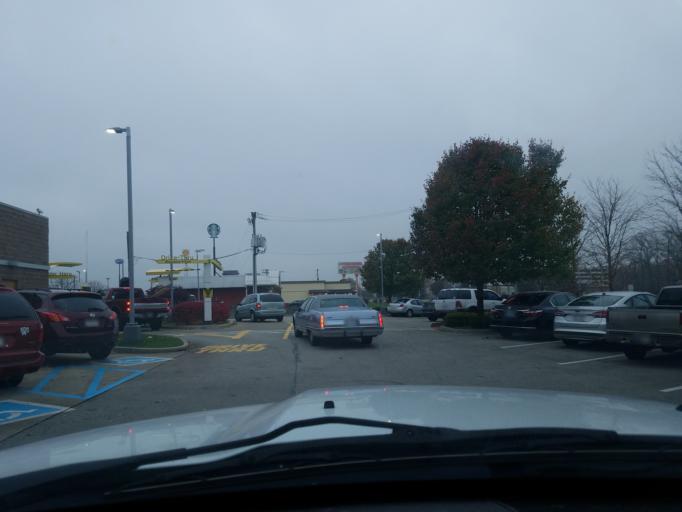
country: US
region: Indiana
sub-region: Bartholomew County
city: Columbus
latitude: 39.2000
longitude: -85.9487
